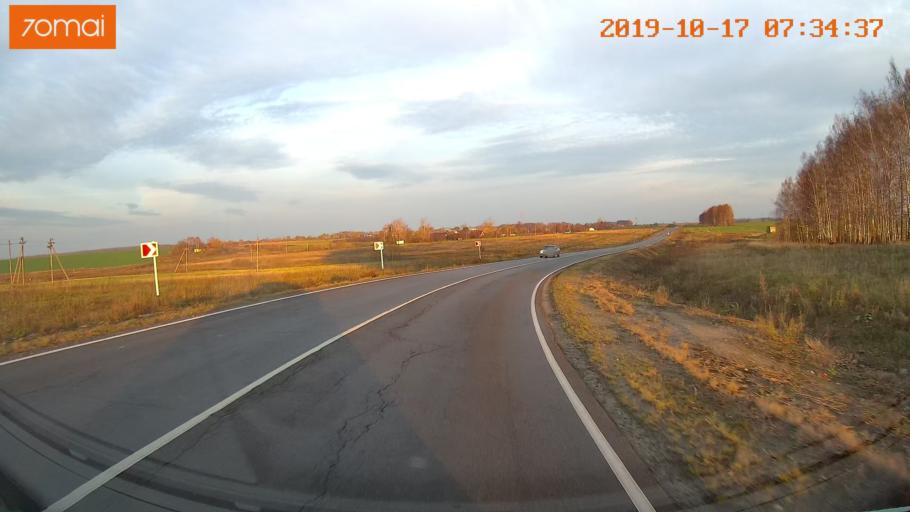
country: RU
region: Ivanovo
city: Gavrilov Posad
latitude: 56.4181
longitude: 39.9376
